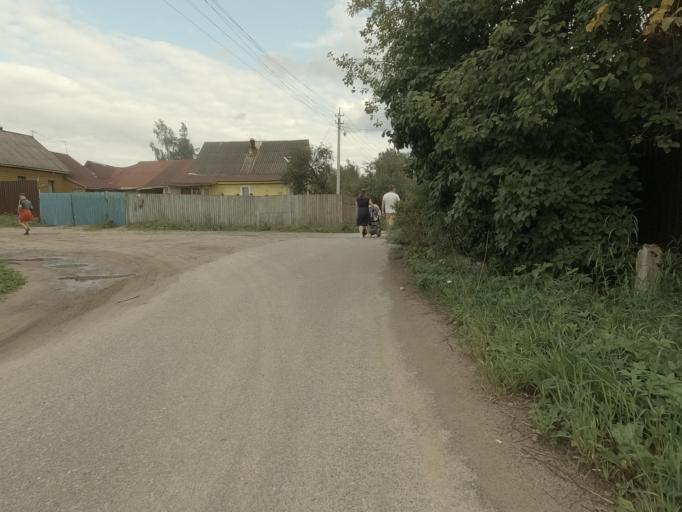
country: RU
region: Leningrad
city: Koltushi
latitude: 59.8986
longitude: 30.6840
